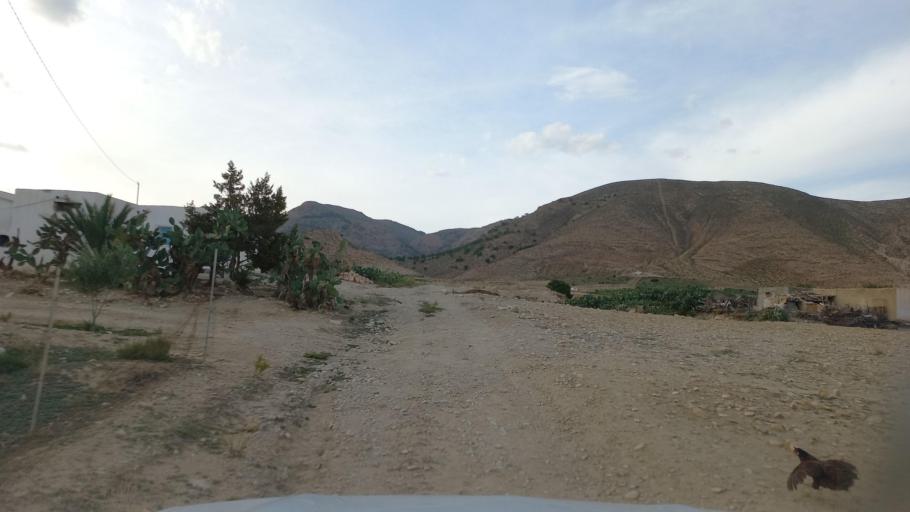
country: TN
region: Al Qasrayn
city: Sbiba
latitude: 35.4504
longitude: 9.0640
